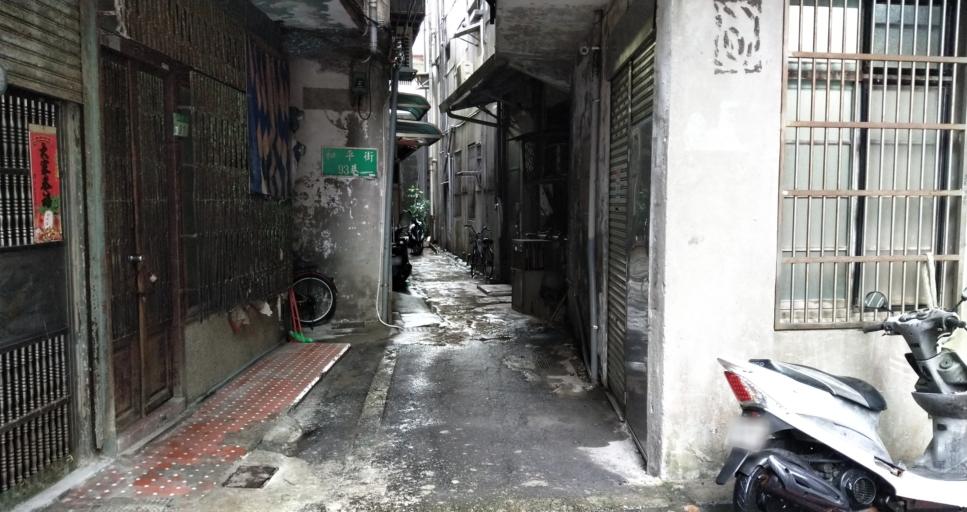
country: TW
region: Taiwan
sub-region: Keelung
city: Keelung
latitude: 25.0702
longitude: 121.6610
